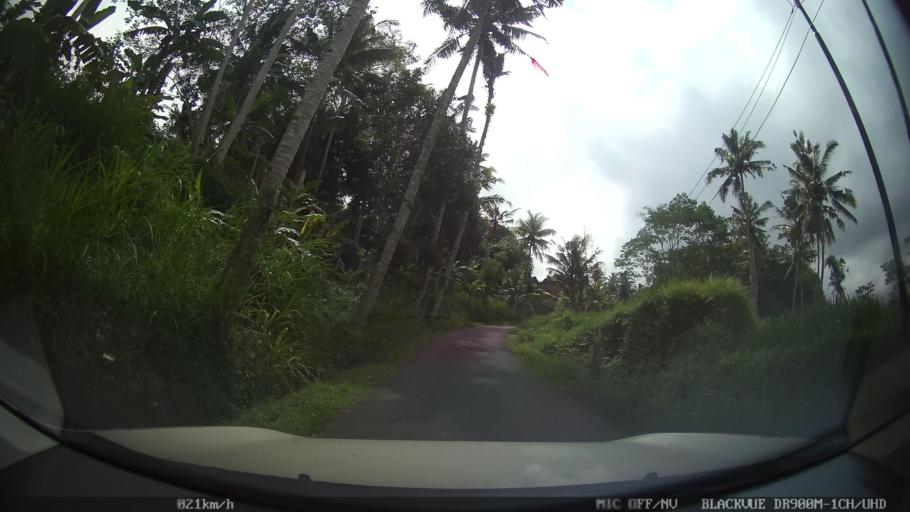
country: ID
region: Bali
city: Banjar Susut Kaja
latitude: -8.4405
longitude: 115.3315
